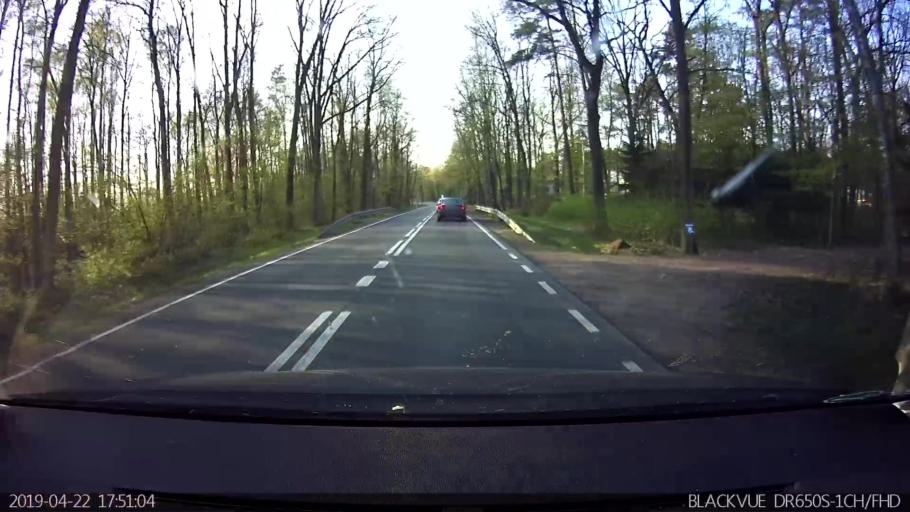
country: PL
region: Masovian Voivodeship
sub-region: Powiat wegrowski
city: Wegrow
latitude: 52.4320
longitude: 21.9971
